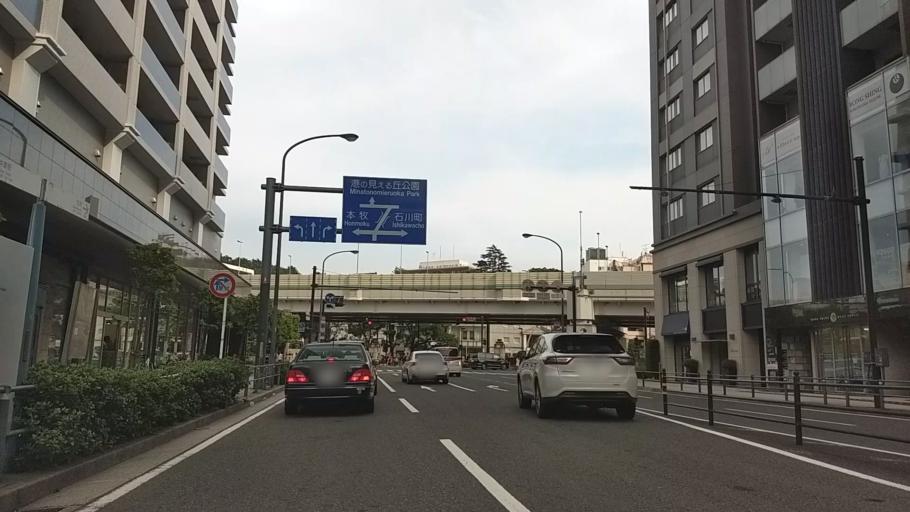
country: JP
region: Kanagawa
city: Yokohama
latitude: 35.4428
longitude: 139.6501
